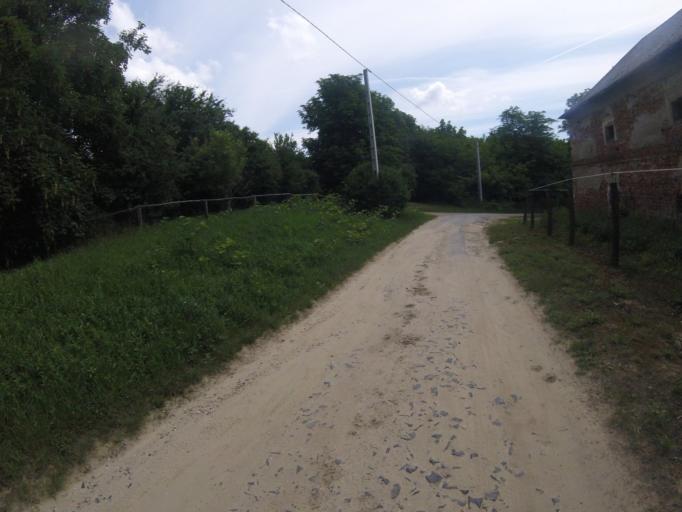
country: HU
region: Zala
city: Zalaszentgrot
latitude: 46.8834
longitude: 17.0358
